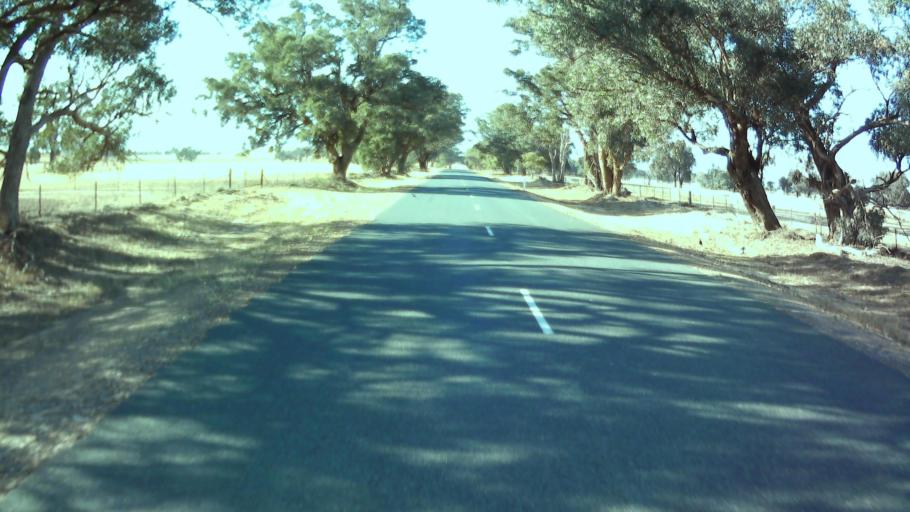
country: AU
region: New South Wales
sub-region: Weddin
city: Grenfell
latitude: -33.9605
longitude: 148.1400
